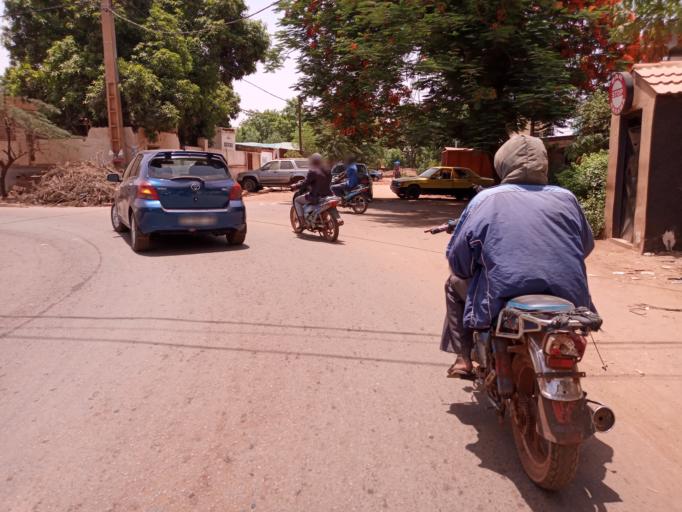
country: ML
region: Bamako
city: Bamako
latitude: 12.6441
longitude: -7.9772
